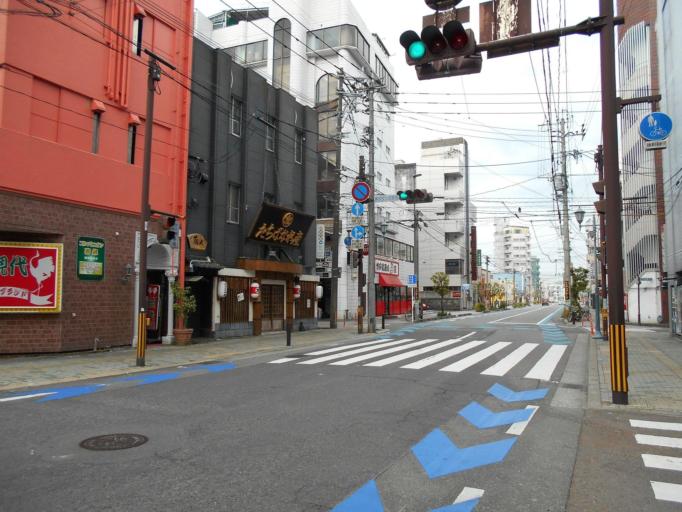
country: JP
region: Miyazaki
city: Miyazaki-shi
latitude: 31.9131
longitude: 131.4214
